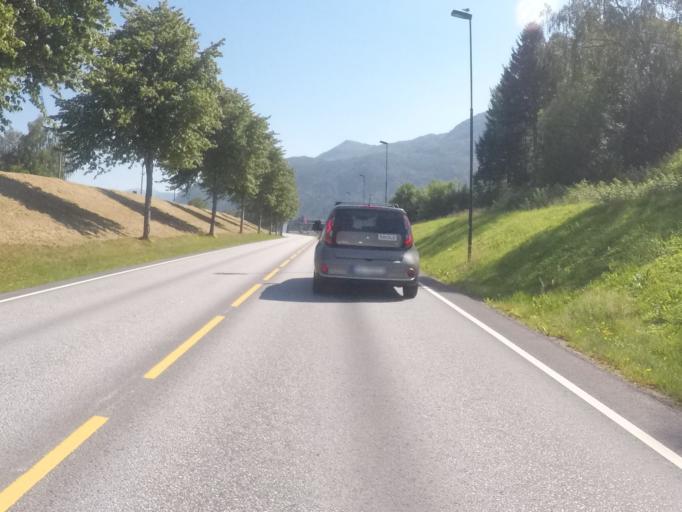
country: NO
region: Sogn og Fjordane
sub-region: Eid
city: Nordfjordeid
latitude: 61.9110
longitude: 5.9926
